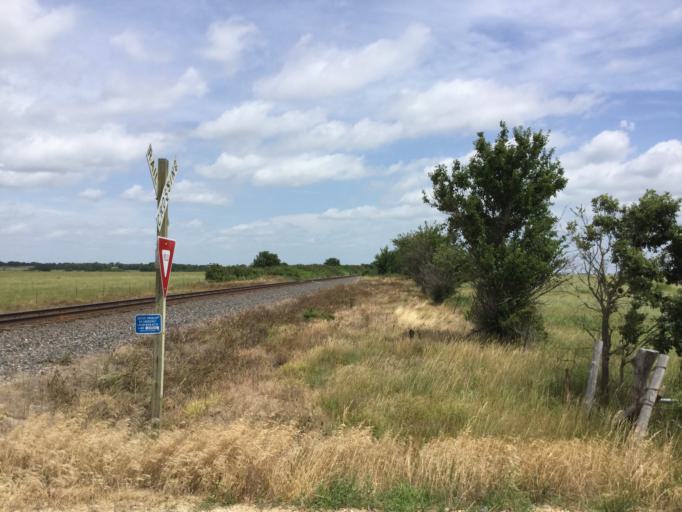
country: US
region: Kansas
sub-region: Woodson County
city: Yates Center
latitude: 37.9226
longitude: -95.6948
